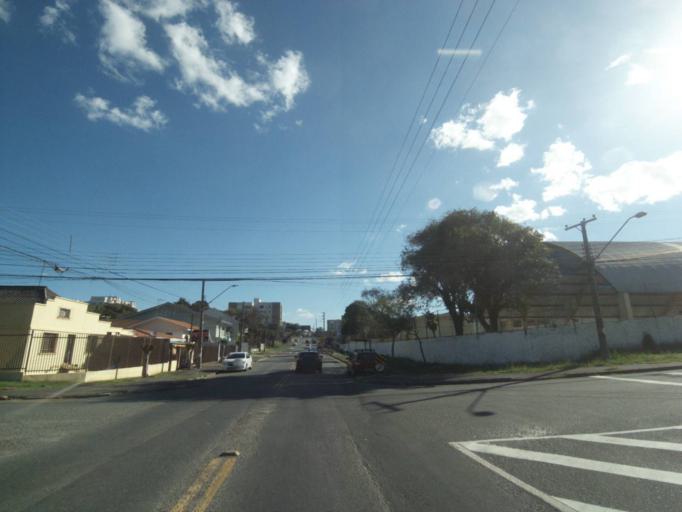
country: BR
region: Parana
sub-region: Curitiba
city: Curitiba
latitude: -25.3925
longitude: -49.2479
